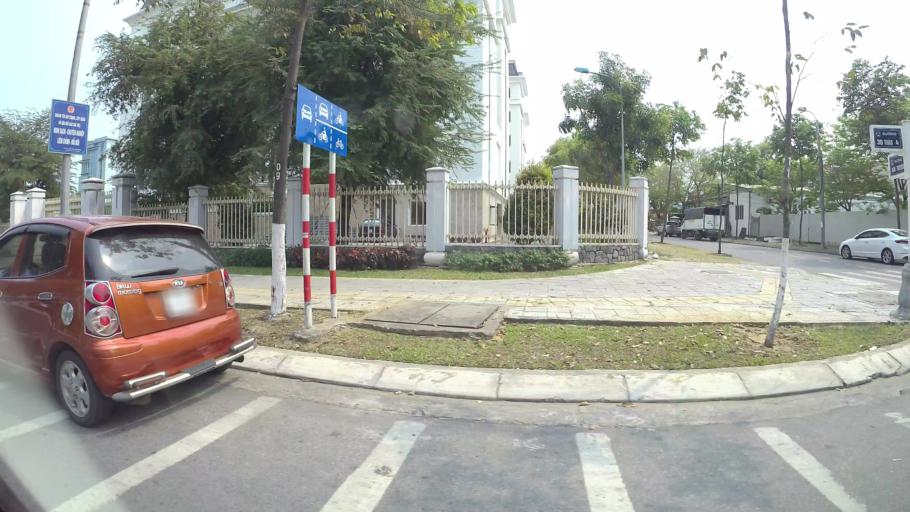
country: VN
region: Da Nang
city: Son Tra
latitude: 16.0404
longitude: 108.2211
